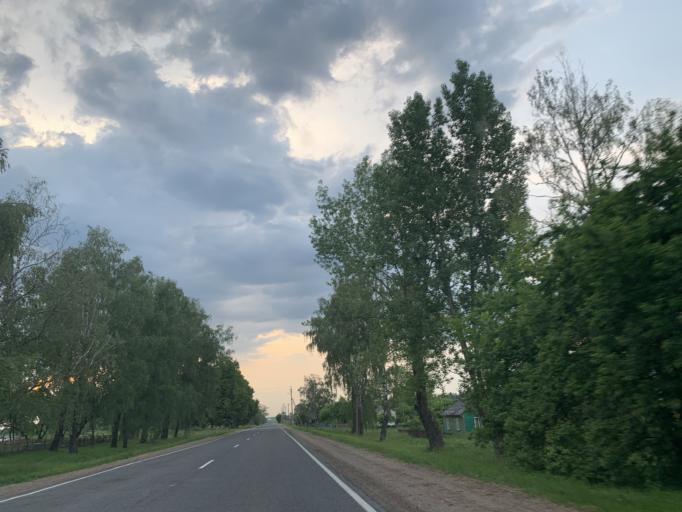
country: BY
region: Minsk
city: Tsimkavichy
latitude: 53.1296
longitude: 26.8778
